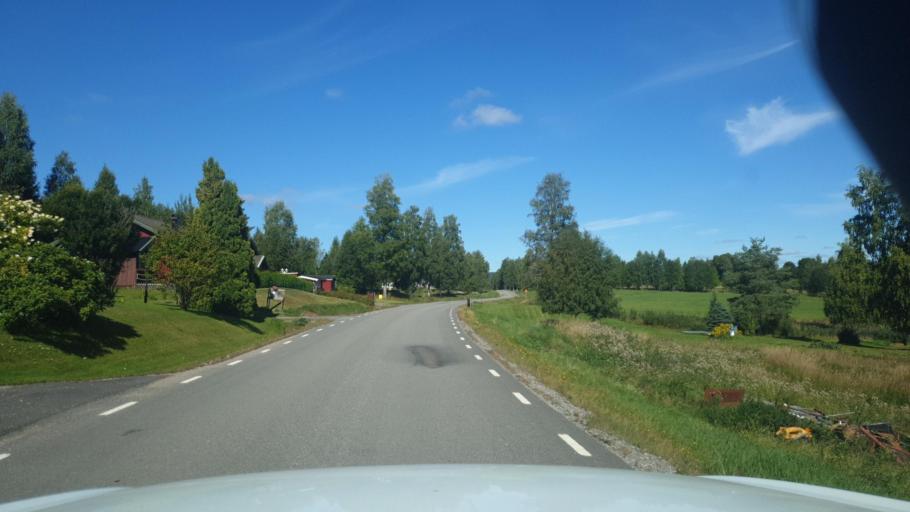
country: SE
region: Vaermland
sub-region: Eda Kommun
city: Charlottenberg
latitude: 59.9463
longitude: 12.5196
